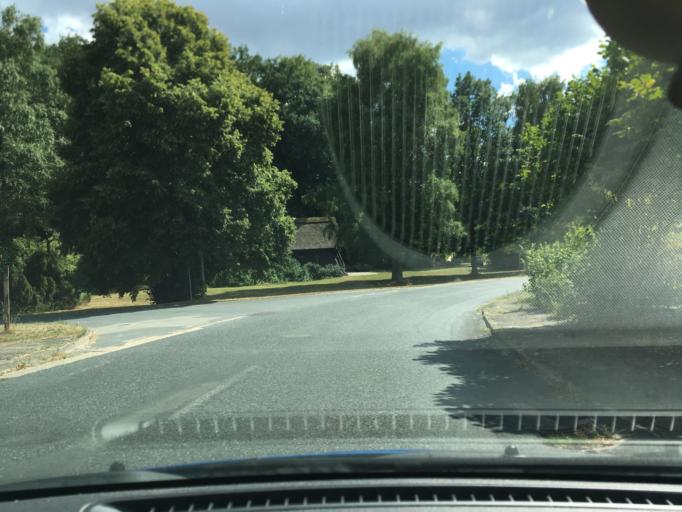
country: DE
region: Lower Saxony
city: Rehlingen
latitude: 53.0629
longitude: 10.2347
